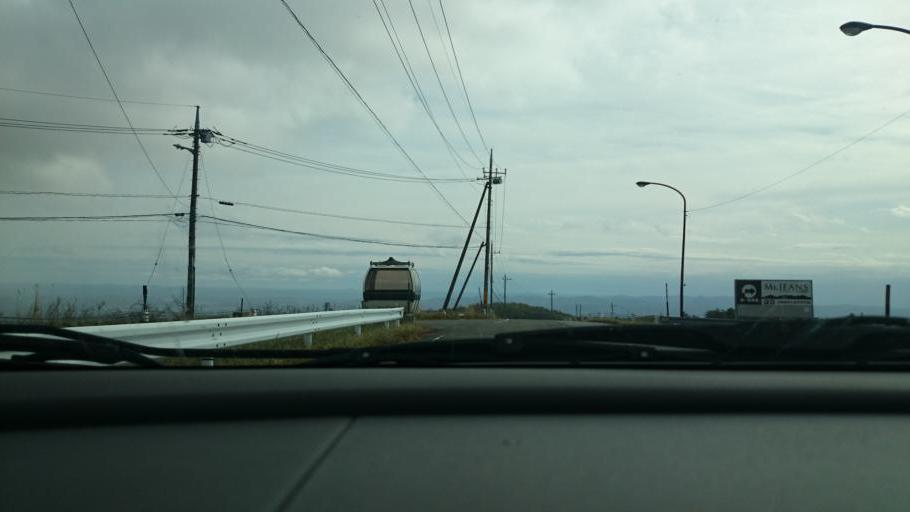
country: JP
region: Tochigi
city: Kuroiso
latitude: 37.1271
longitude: 140.0165
